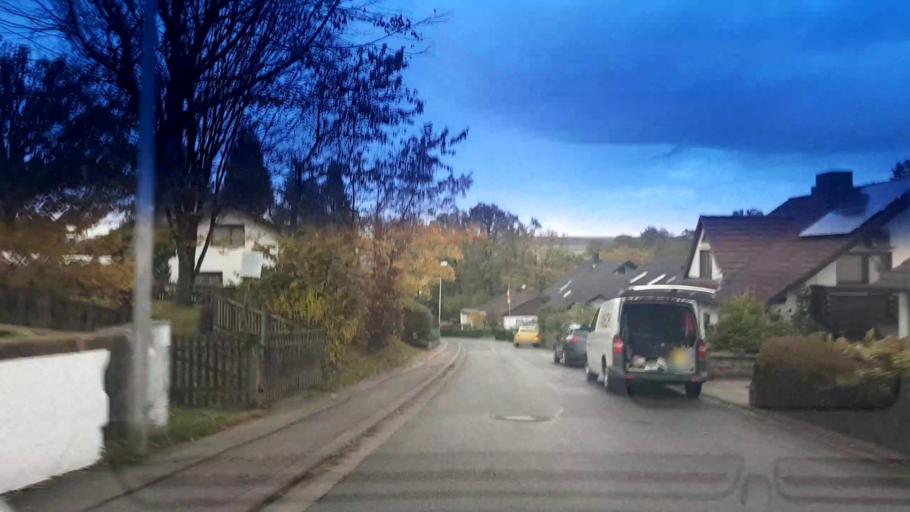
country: DE
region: Bavaria
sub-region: Upper Franconia
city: Viereth-Trunstadt
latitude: 49.9182
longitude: 10.7765
